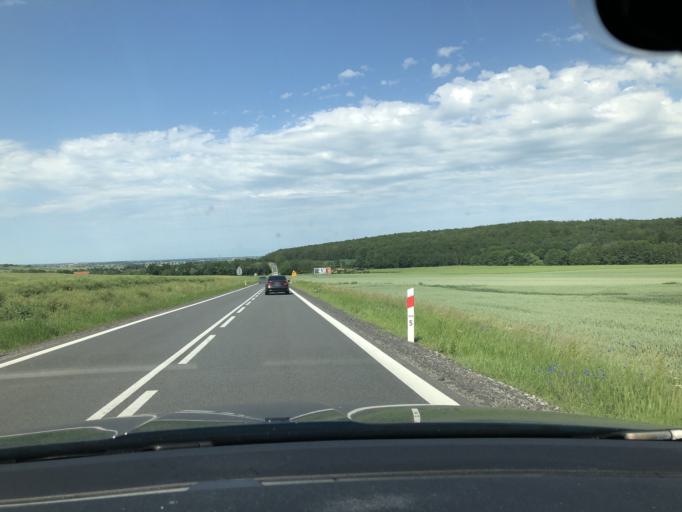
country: PL
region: Lower Silesian Voivodeship
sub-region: Powiat jaworski
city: Bolkow
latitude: 50.9565
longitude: 16.1430
